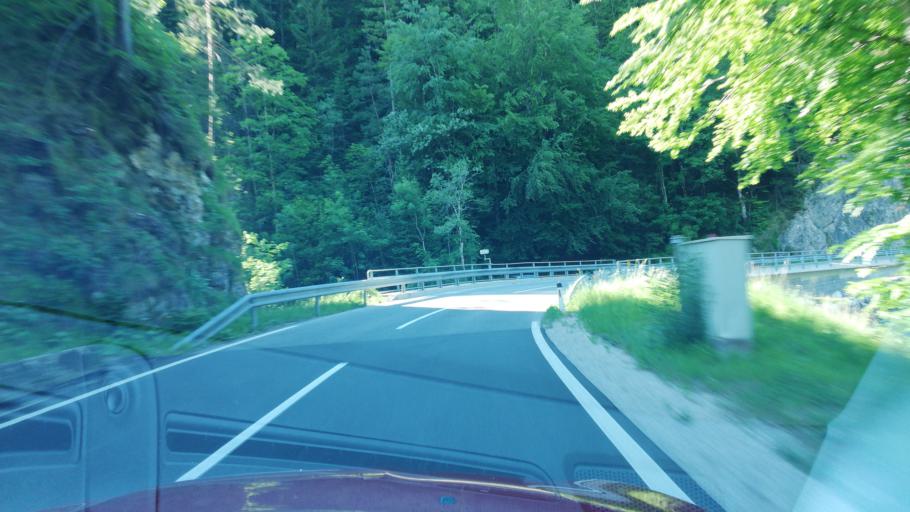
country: AT
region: Upper Austria
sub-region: Politischer Bezirk Kirchdorf an der Krems
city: Rossleithen
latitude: 47.7575
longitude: 14.1634
